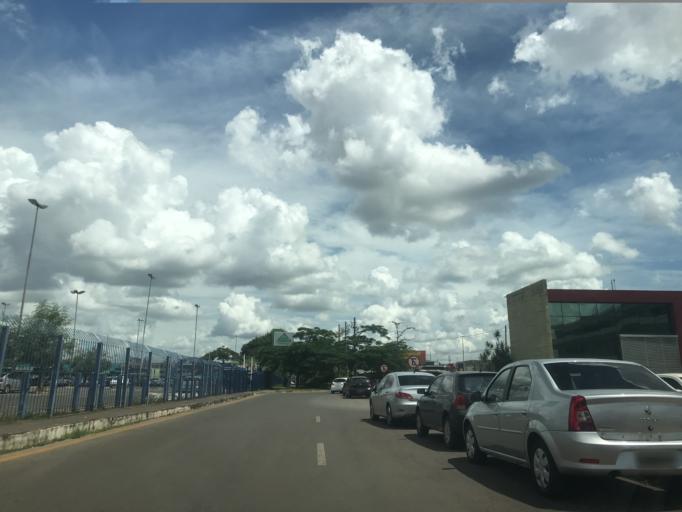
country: BR
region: Federal District
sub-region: Brasilia
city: Brasilia
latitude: -15.8437
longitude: -48.0434
